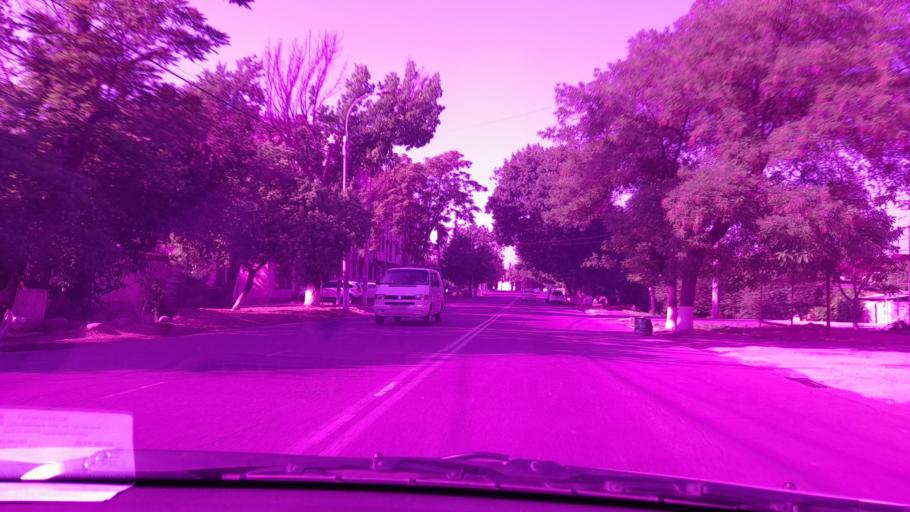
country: UZ
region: Toshkent
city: Salor
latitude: 41.3255
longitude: 69.3485
